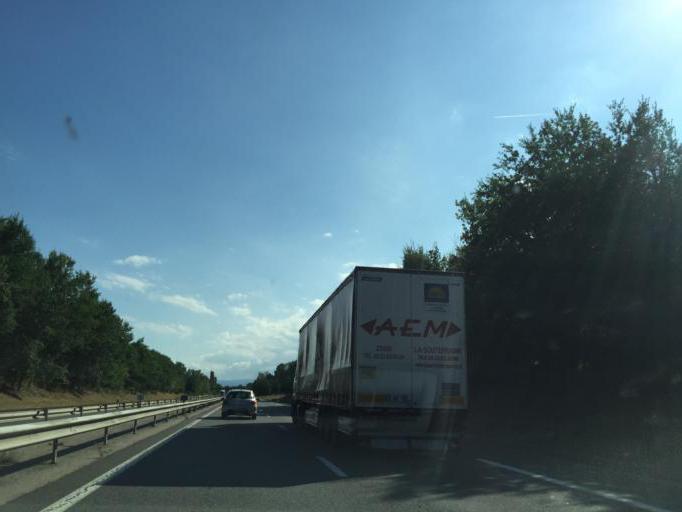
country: FR
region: Rhone-Alpes
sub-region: Departement de la Loire
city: Feurs
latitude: 45.7109
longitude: 4.1687
